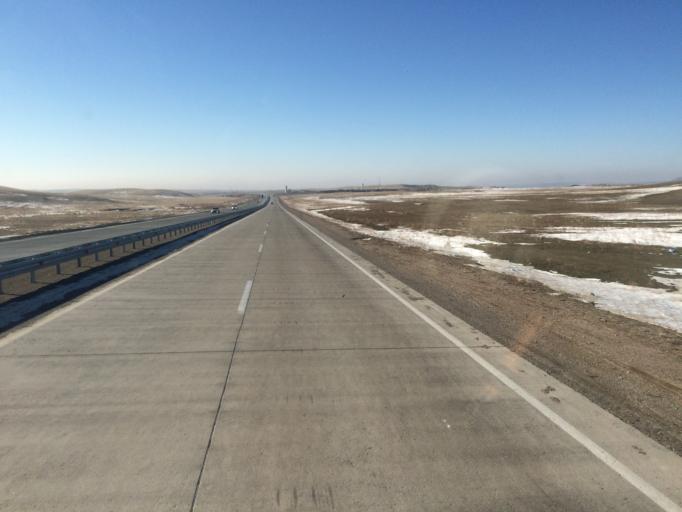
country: KZ
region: Zhambyl
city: Georgiyevka
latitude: 43.3564
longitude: 74.5854
